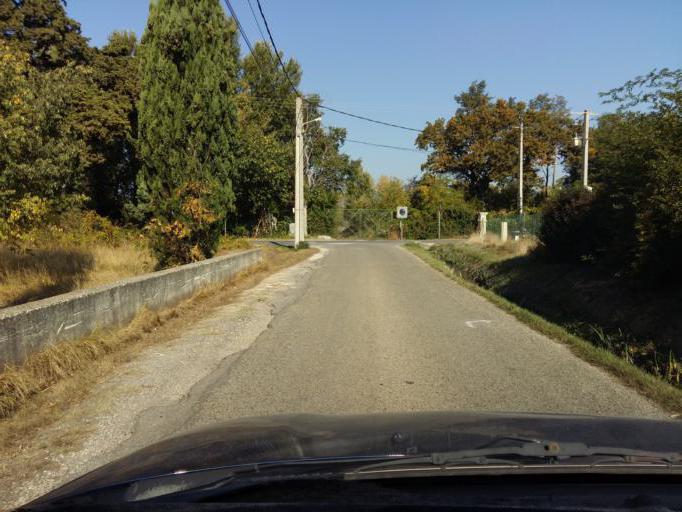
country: FR
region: Provence-Alpes-Cote d'Azur
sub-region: Departement du Vaucluse
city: Camaret-sur-Aigues
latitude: 44.1737
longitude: 4.8725
